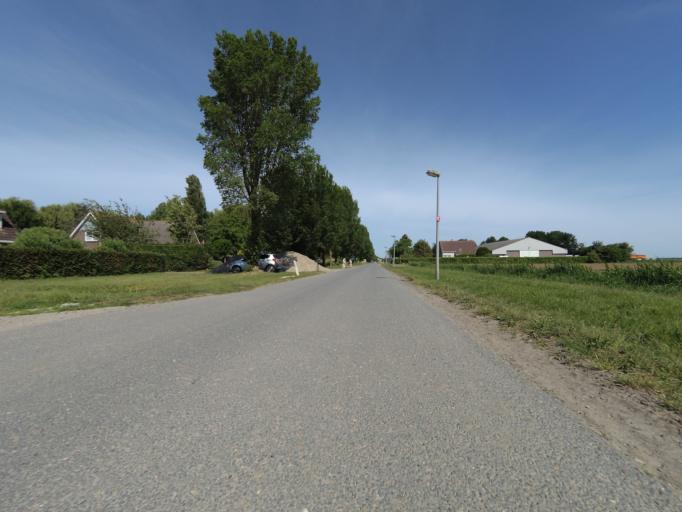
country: NL
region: North Holland
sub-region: Gemeente Huizen
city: Huizen
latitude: 52.3522
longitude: 5.3188
